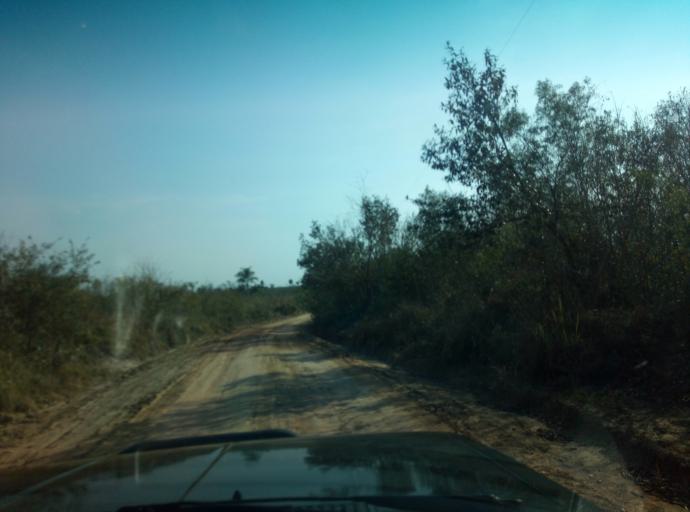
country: PY
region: Caaguazu
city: Doctor Cecilio Baez
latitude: -25.1881
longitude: -56.1918
